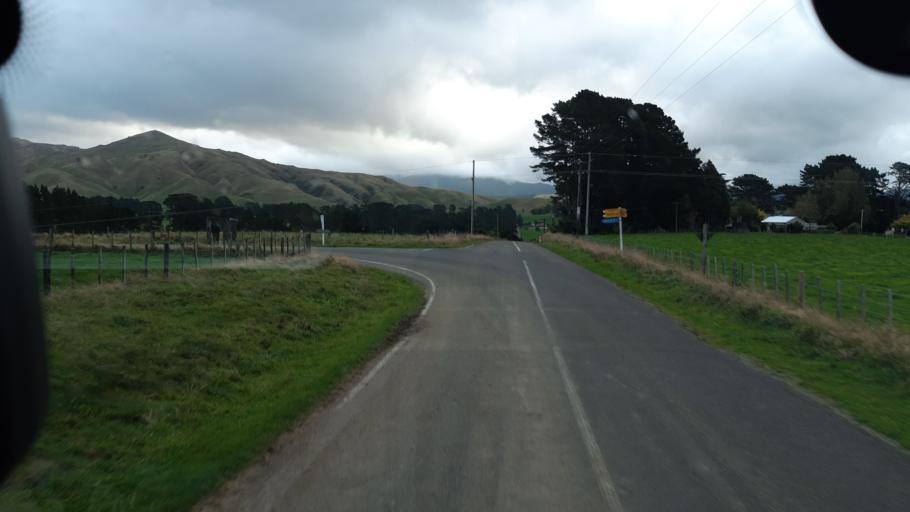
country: NZ
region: Manawatu-Wanganui
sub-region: Palmerston North City
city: Palmerston North
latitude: -40.6440
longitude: 175.6525
